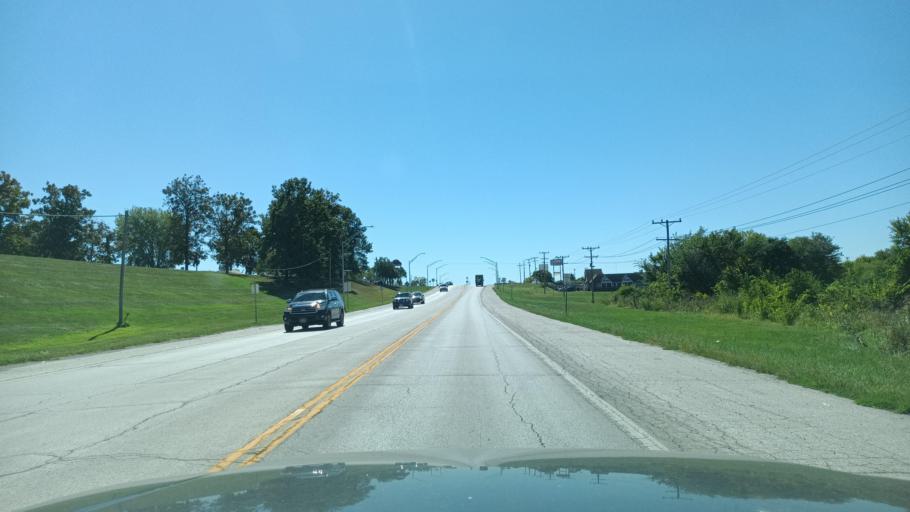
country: US
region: Missouri
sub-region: Adair County
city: Kirksville
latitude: 40.1736
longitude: -92.5720
